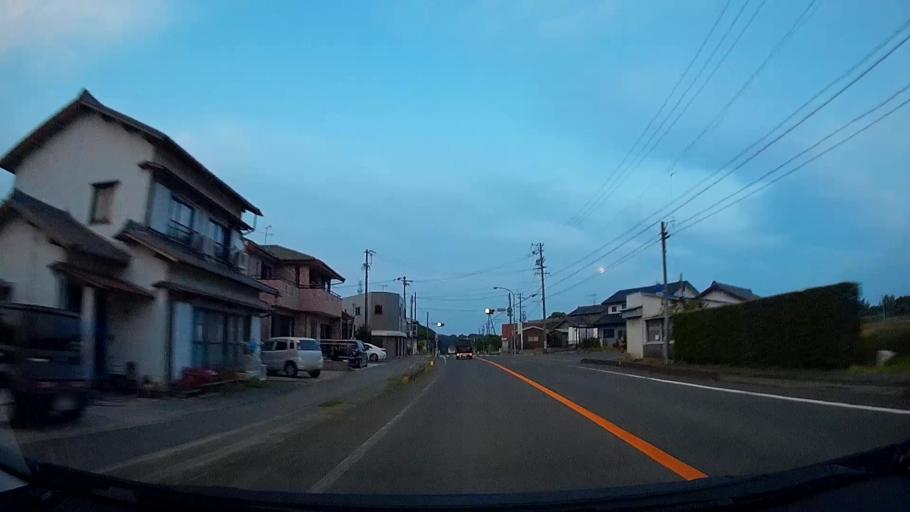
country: JP
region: Shizuoka
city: Kosai-shi
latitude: 34.6843
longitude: 137.5030
